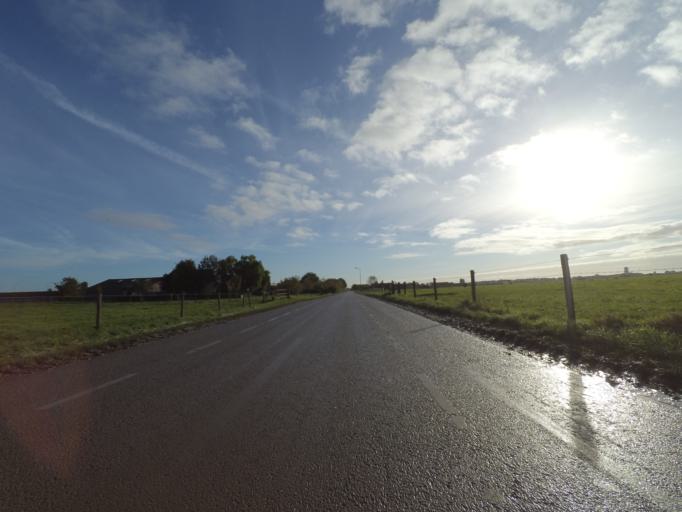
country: NL
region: Utrecht
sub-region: Gemeente Utrechtse Heuvelrug
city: Driebergen-Rijsenburg
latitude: 52.0163
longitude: 5.2490
